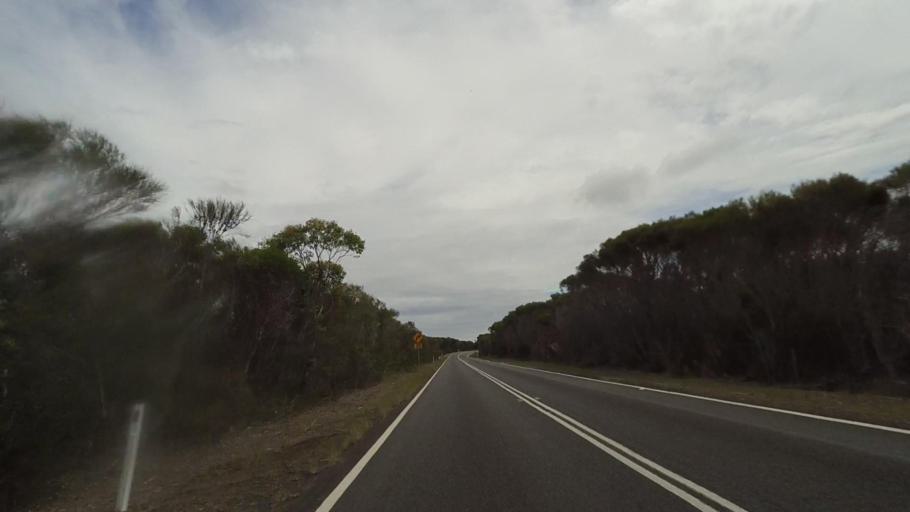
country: AU
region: New South Wales
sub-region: Sutherland Shire
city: Bundeena
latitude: -34.1002
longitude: 151.1226
